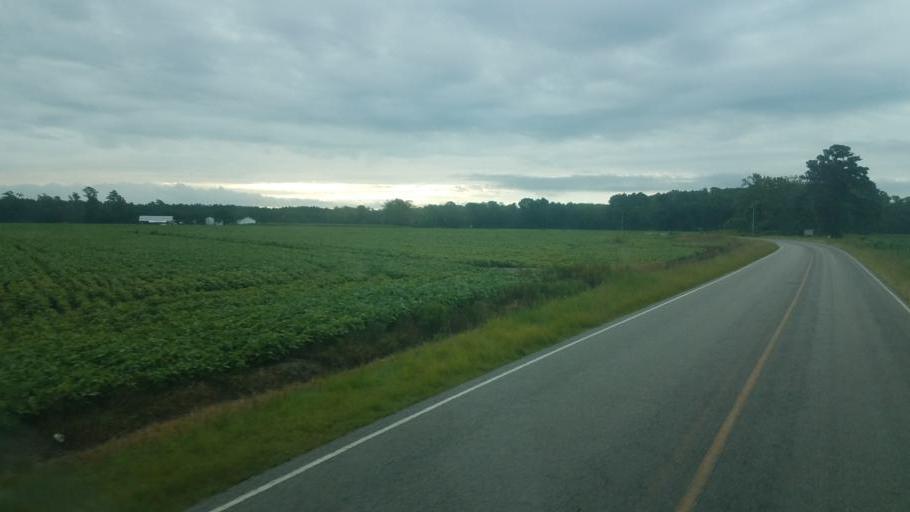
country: US
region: North Carolina
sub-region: Tyrrell County
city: Columbia
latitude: 35.9376
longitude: -76.2782
